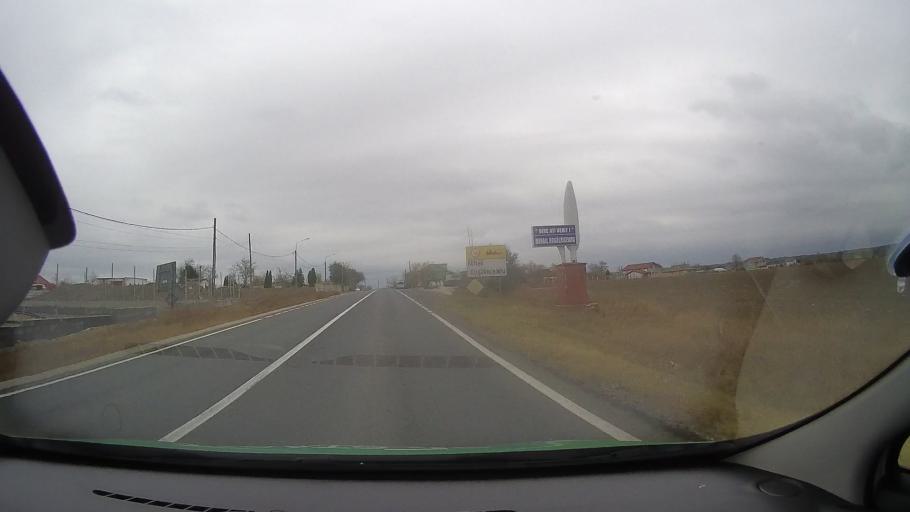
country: RO
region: Constanta
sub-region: Comuna Mihail Kogalniceanu
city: Mihail Kogalniceanu
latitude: 44.3683
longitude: 28.4512
